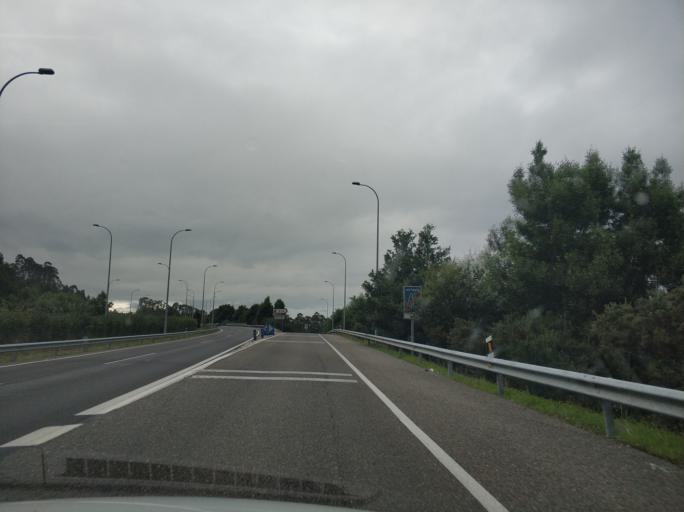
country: ES
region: Galicia
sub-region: Provincia de Lugo
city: Barreiros
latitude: 43.5365
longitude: -7.1480
